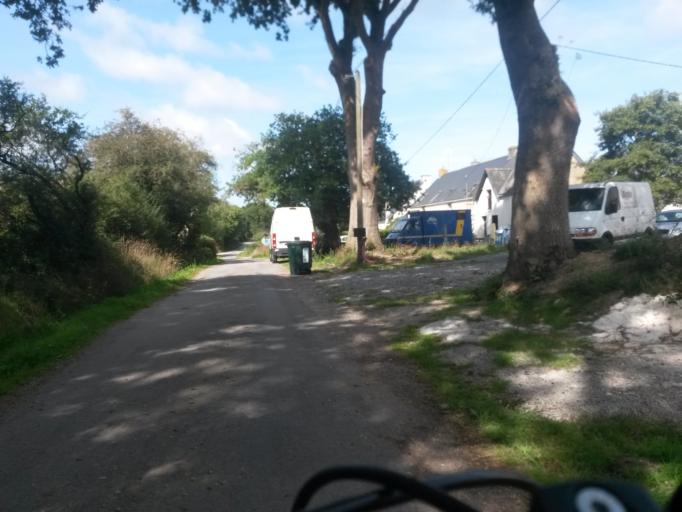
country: FR
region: Pays de la Loire
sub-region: Departement de la Loire-Atlantique
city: Asserac
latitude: 47.3889
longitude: -2.3666
